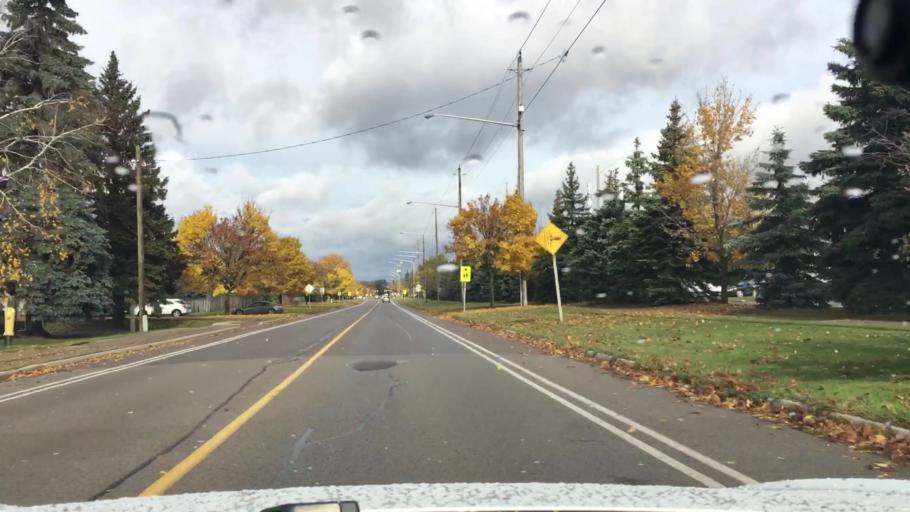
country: CA
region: Ontario
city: Oshawa
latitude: 43.9037
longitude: -78.7851
